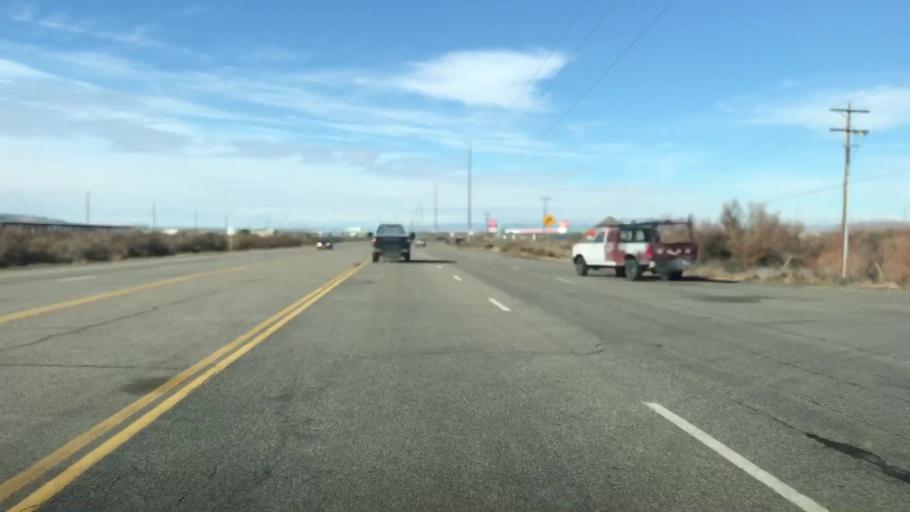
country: US
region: Colorado
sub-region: Mesa County
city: Redlands
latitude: 39.1066
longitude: -108.6381
